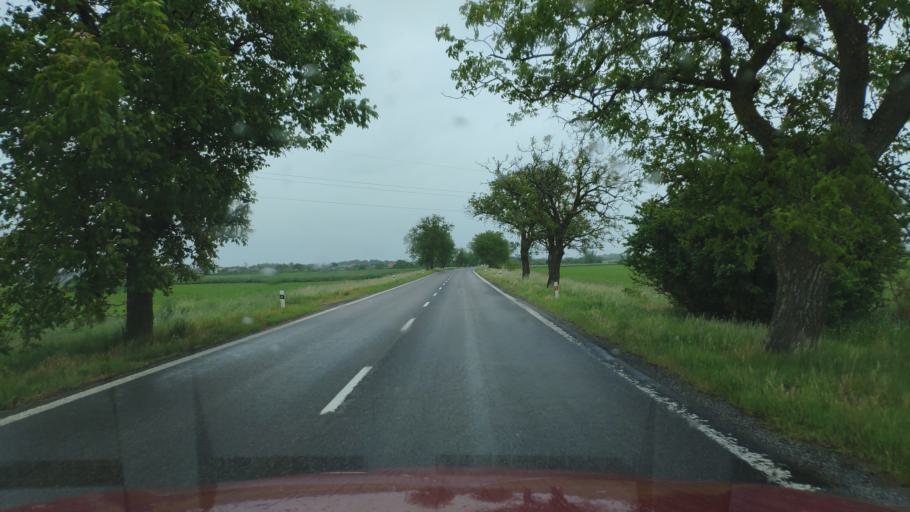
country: HU
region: Borsod-Abauj-Zemplen
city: Karcsa
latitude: 48.4221
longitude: 21.8377
